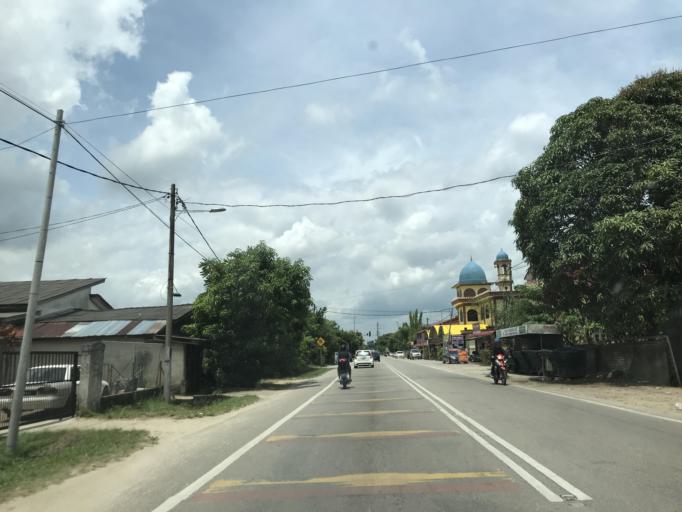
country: MY
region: Kelantan
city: Kota Bharu
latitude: 6.1012
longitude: 102.2104
